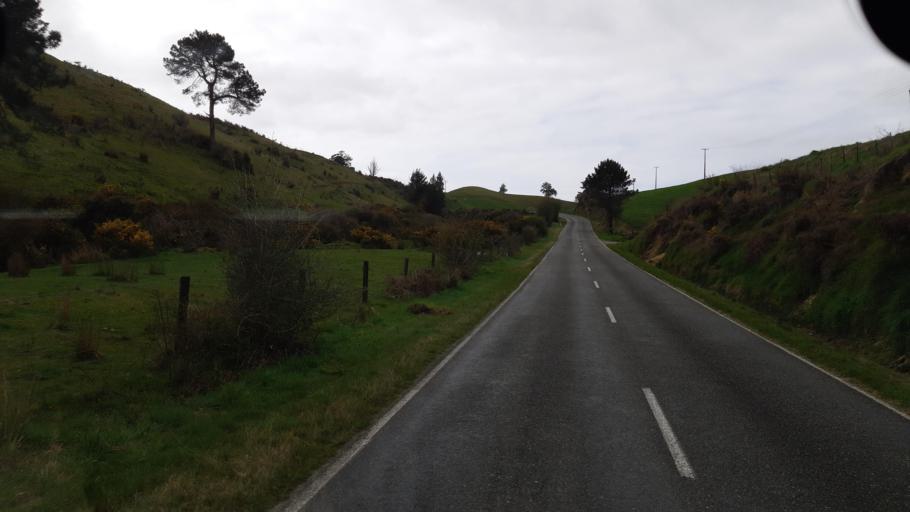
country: NZ
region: Tasman
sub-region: Tasman District
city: Motueka
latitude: -41.2753
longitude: 172.9332
